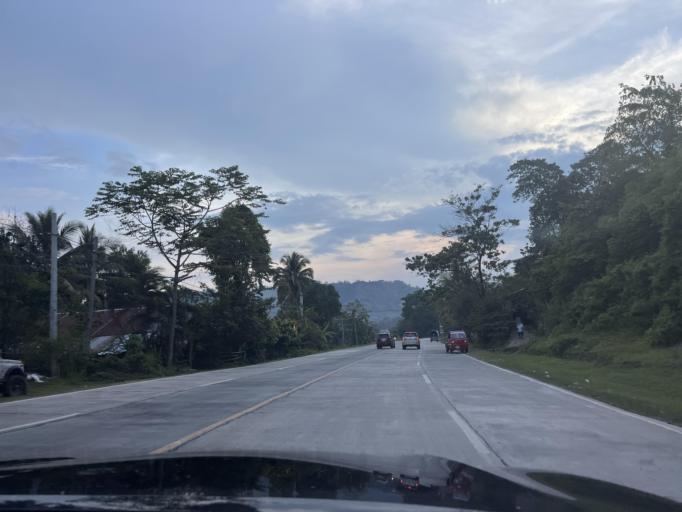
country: PH
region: Northern Mindanao
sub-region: Province of Bukidnon
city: Dalorong
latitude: 7.6108
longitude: 125.1190
